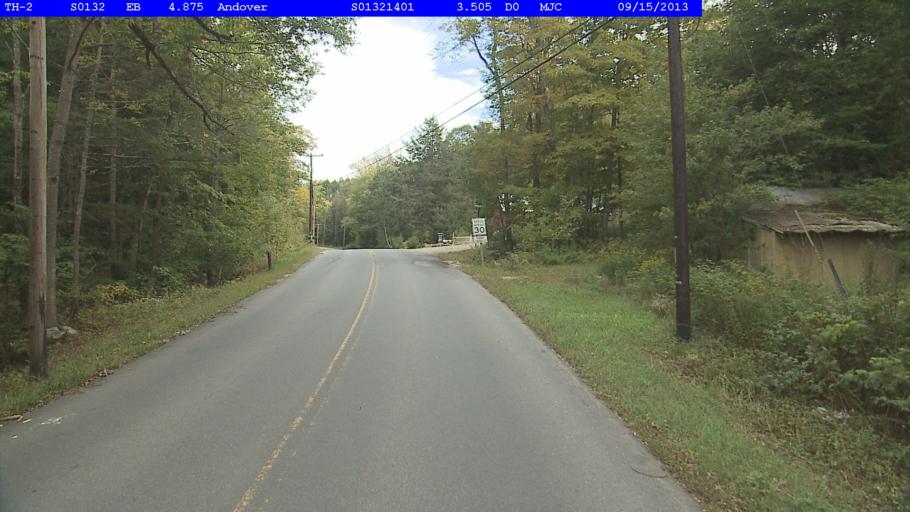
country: US
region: Vermont
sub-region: Windsor County
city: Chester
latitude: 43.2793
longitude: -72.7063
